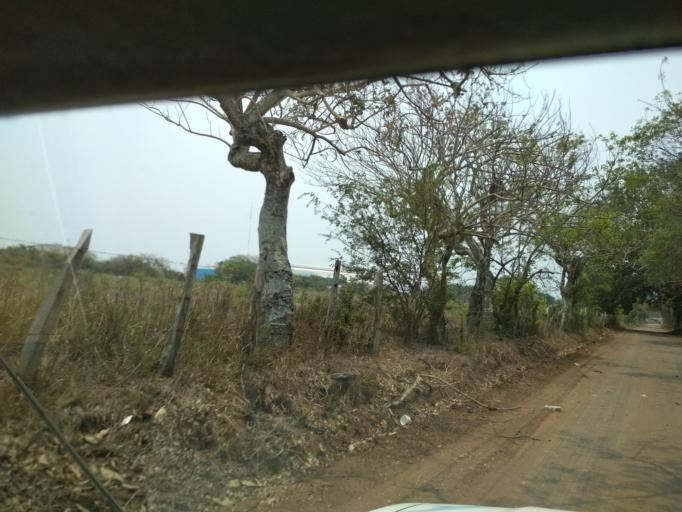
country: MX
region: Veracruz
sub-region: Veracruz
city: Oasis
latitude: 19.1948
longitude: -96.2445
